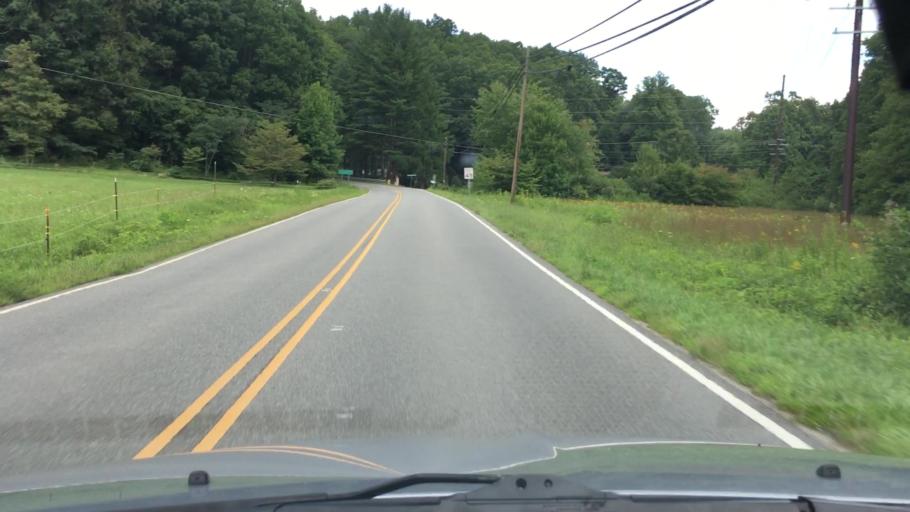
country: US
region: North Carolina
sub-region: Yancey County
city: Burnsville
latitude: 35.8318
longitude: -82.1847
